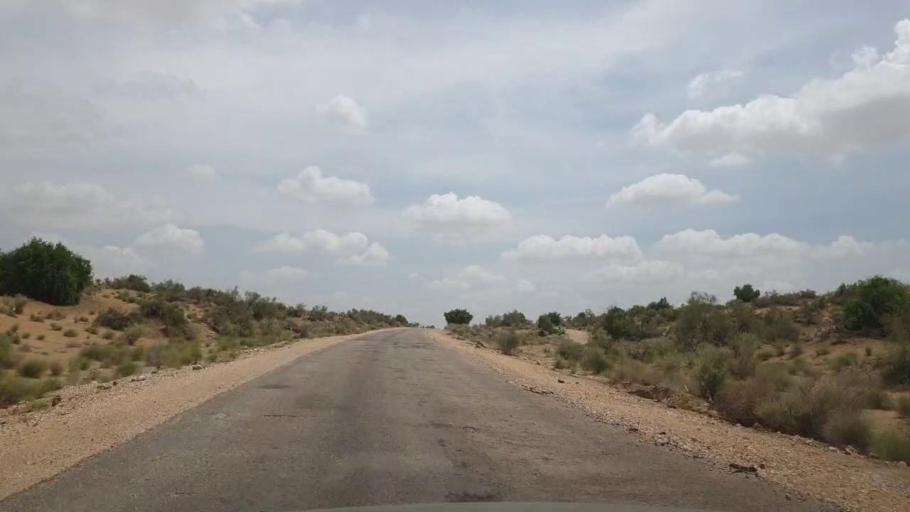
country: PK
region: Sindh
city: Kot Diji
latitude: 27.1612
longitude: 69.2233
